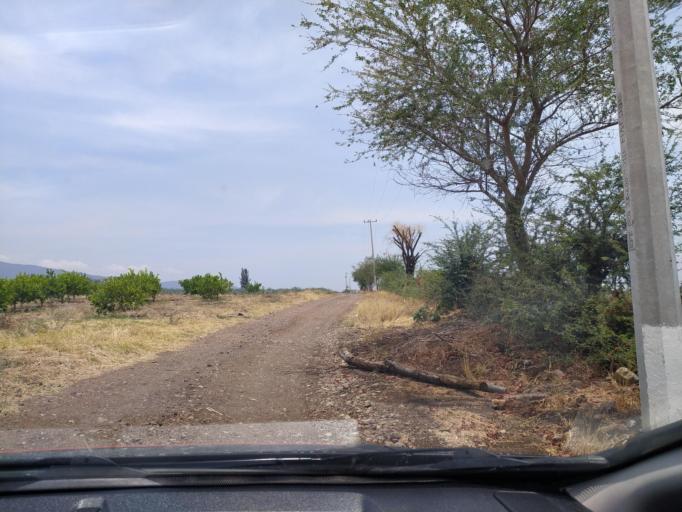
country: MX
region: Jalisco
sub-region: Zacoalco de Torres
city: Barranca de Otates (Barranca de Otatan)
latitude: 20.2688
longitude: -103.6291
